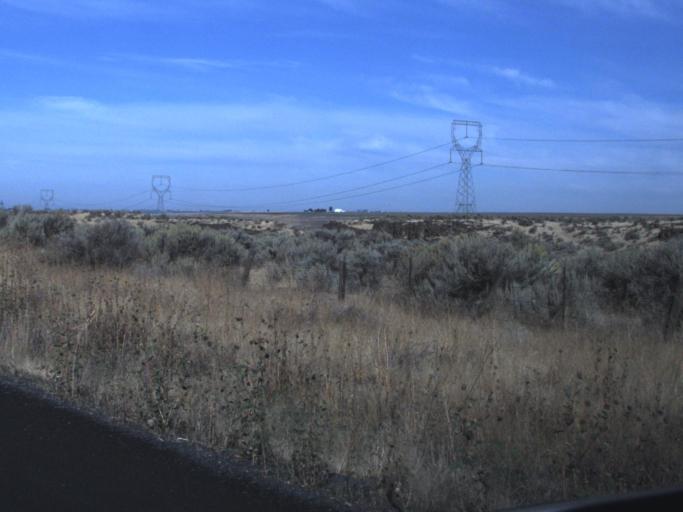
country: US
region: Washington
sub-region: Franklin County
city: Connell
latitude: 46.6312
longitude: -118.7460
